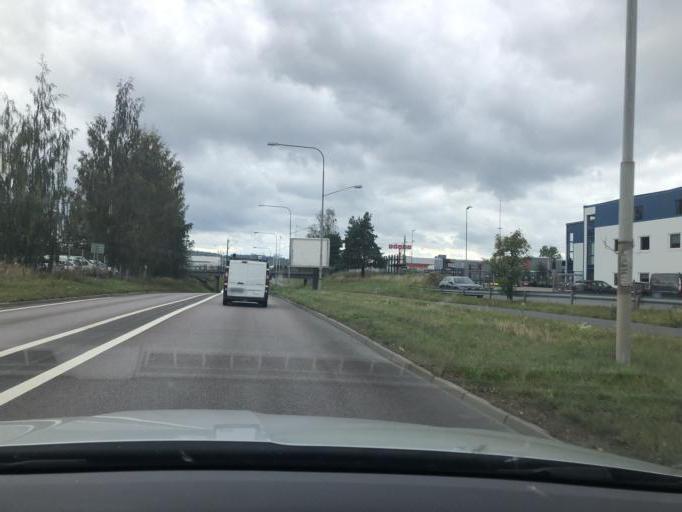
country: SE
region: Joenkoeping
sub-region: Jonkopings Kommun
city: Jonkoping
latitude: 57.7642
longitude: 14.1843
